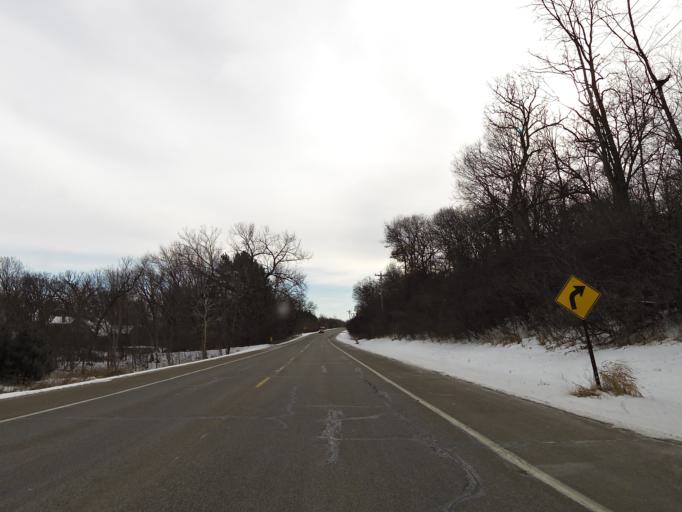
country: US
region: Minnesota
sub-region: Washington County
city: Lakeland
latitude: 44.9727
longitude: -92.7937
